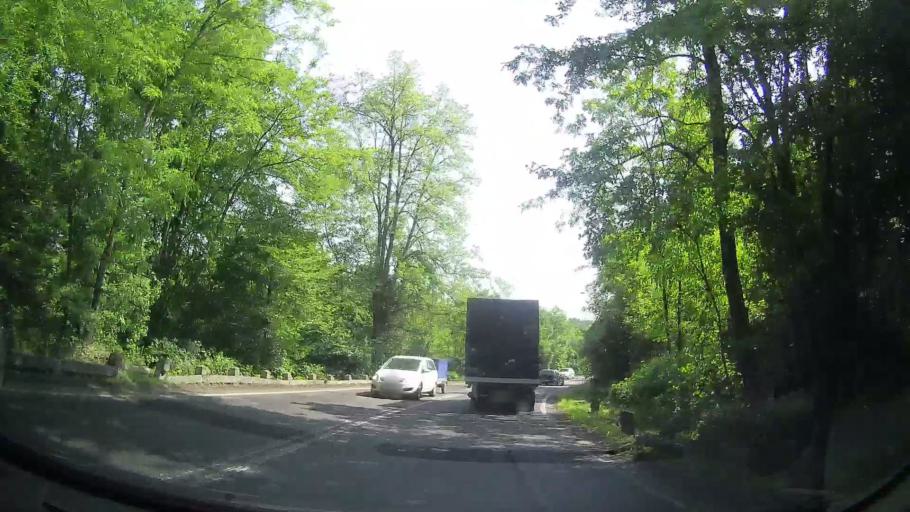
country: RO
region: Timis
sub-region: Comuna Pietroasa
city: Pietroasa
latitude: 45.8756
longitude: 22.3728
